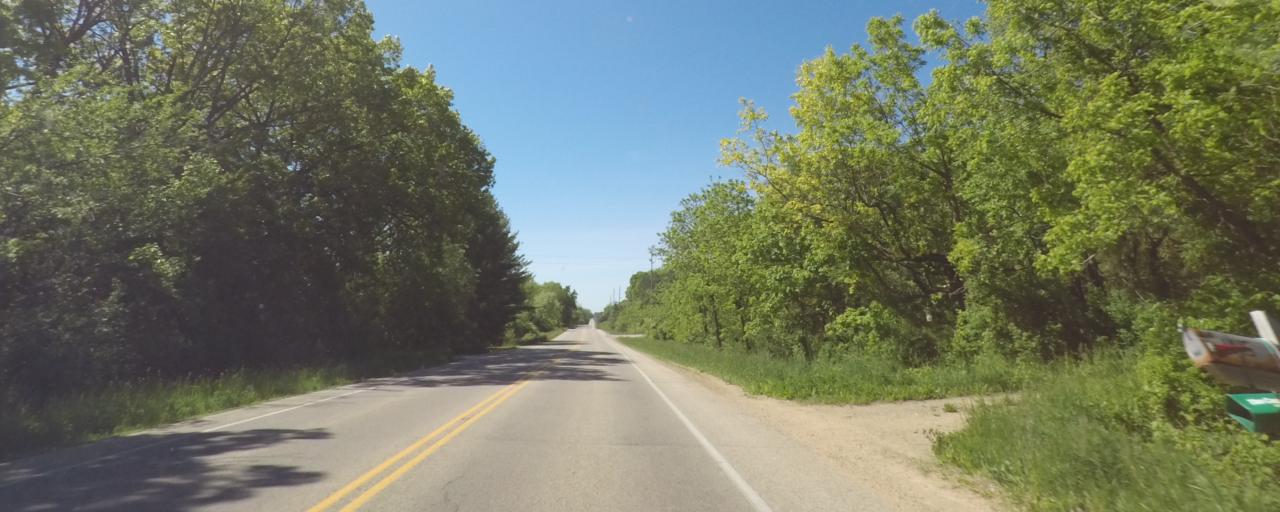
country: US
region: Wisconsin
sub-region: Green County
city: Brooklyn
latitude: 42.8776
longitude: -89.3691
